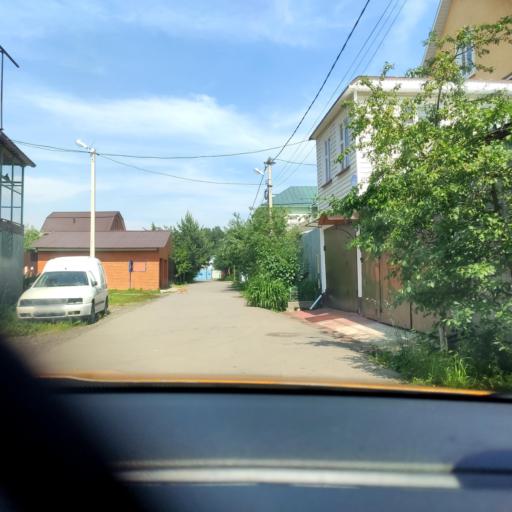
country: RU
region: Moscow
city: Severnyy
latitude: 55.9600
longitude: 37.5433
